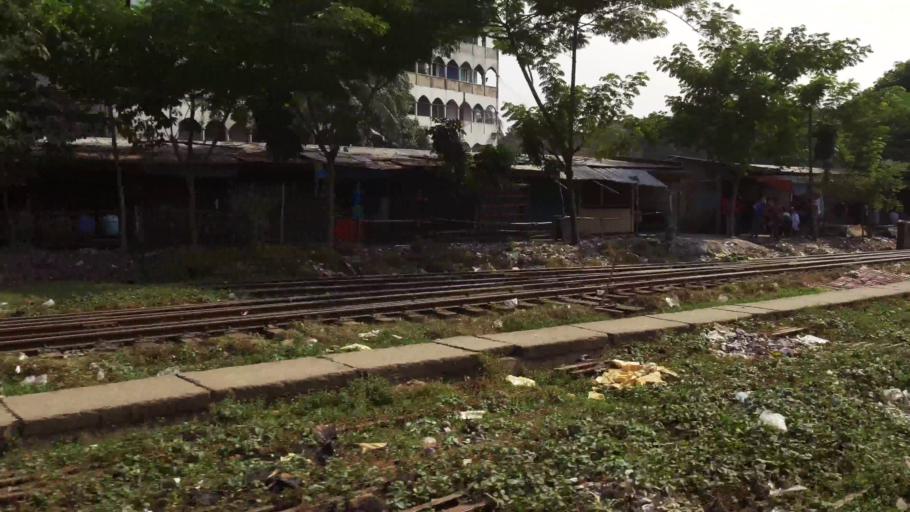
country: BD
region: Dhaka
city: Paltan
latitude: 23.7662
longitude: 90.3958
